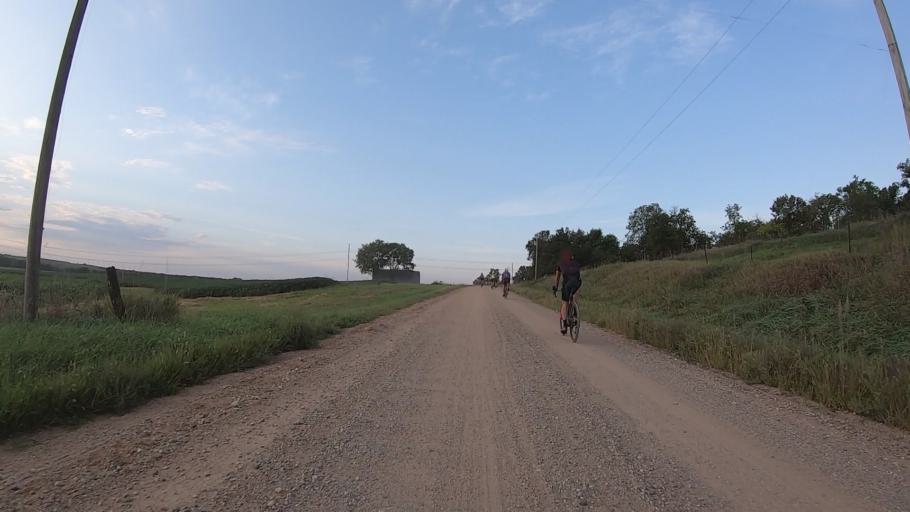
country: US
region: Kansas
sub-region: Marshall County
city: Marysville
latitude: 39.8219
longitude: -96.6667
